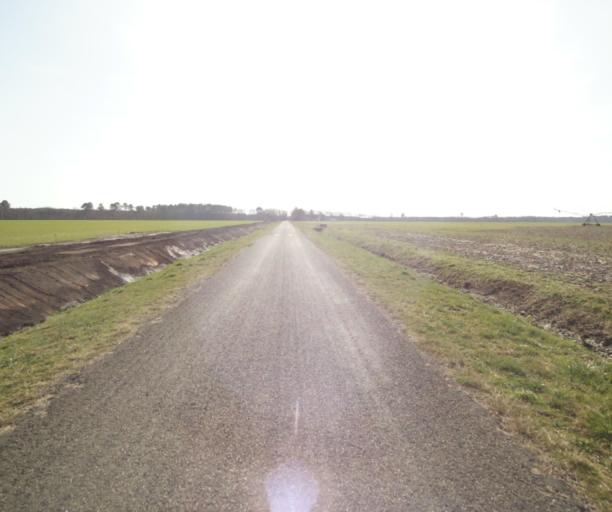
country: FR
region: Aquitaine
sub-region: Departement des Landes
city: Roquefort
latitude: 44.1522
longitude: -0.1715
